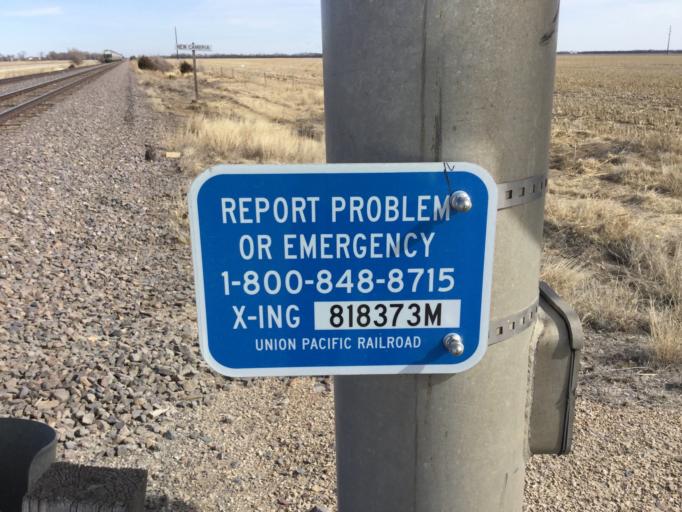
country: US
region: Kansas
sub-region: Saline County
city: Salina
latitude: 38.8812
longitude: -97.5017
